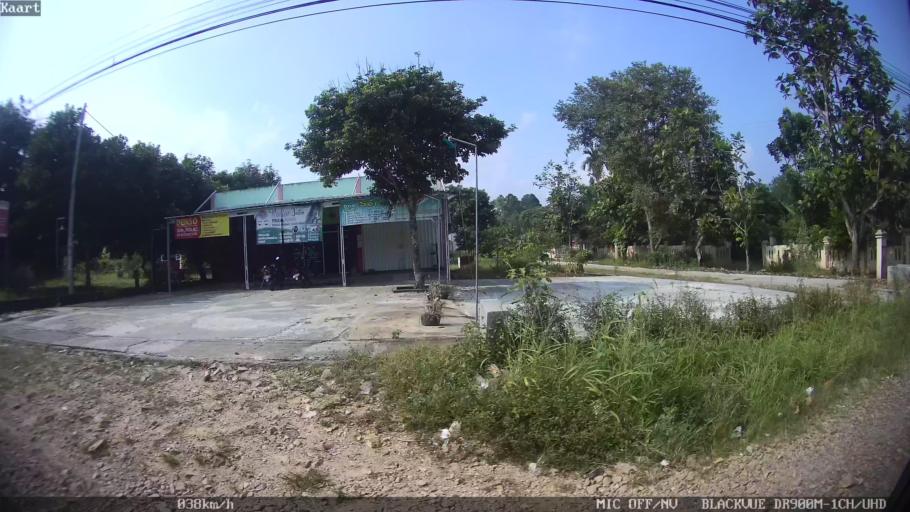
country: ID
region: Lampung
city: Gedongtataan
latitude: -5.3658
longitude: 105.1481
